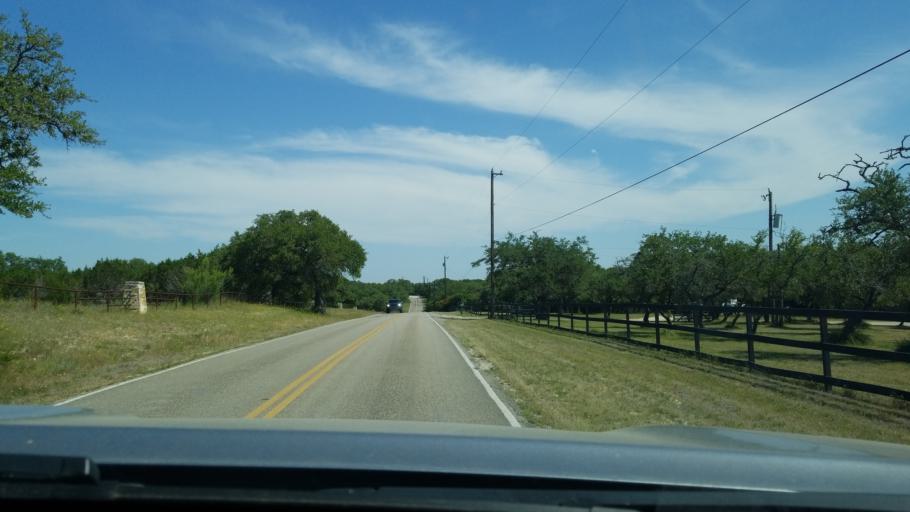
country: US
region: Texas
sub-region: Comal County
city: Bulverde
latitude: 29.7629
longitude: -98.5099
